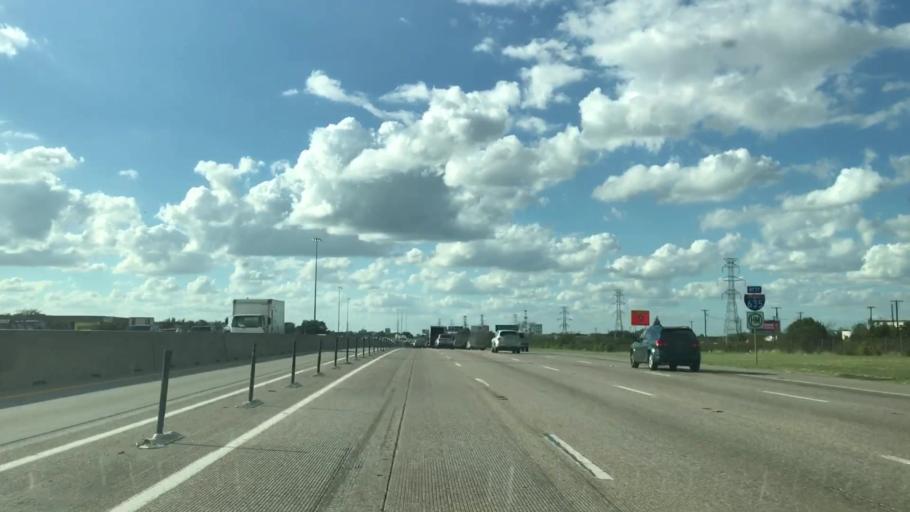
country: US
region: Texas
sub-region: Dallas County
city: Garland
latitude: 32.8813
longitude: -96.6924
